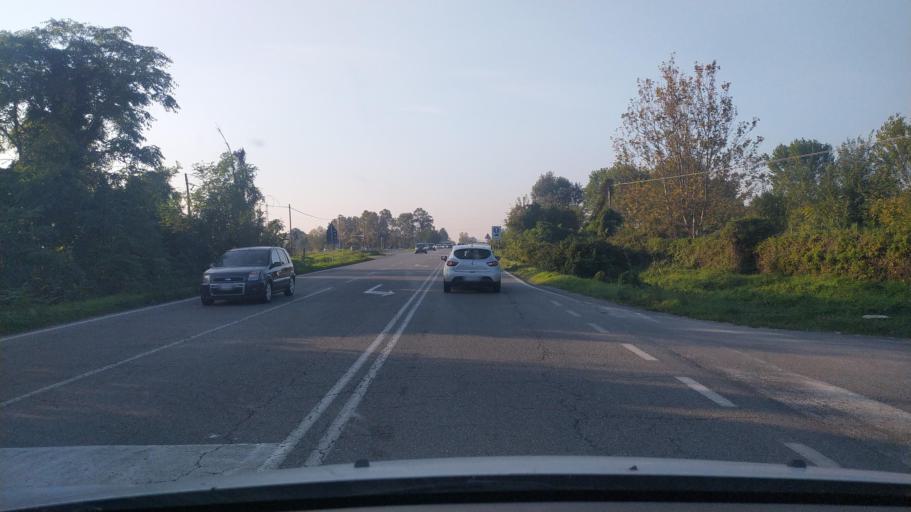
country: IT
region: Lombardy
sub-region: Provincia di Lodi
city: Zelo Buon Persico
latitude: 45.4061
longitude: 9.4478
